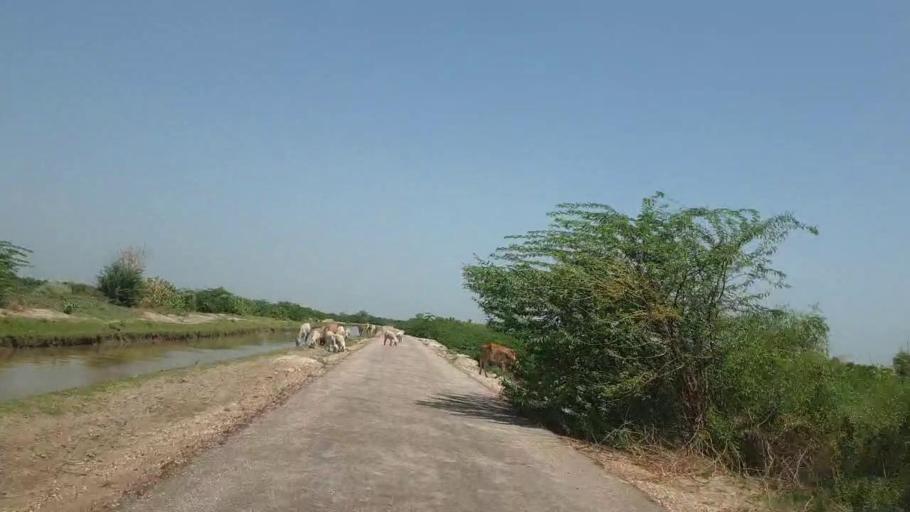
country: PK
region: Sindh
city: Rohri
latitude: 27.6238
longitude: 69.0978
